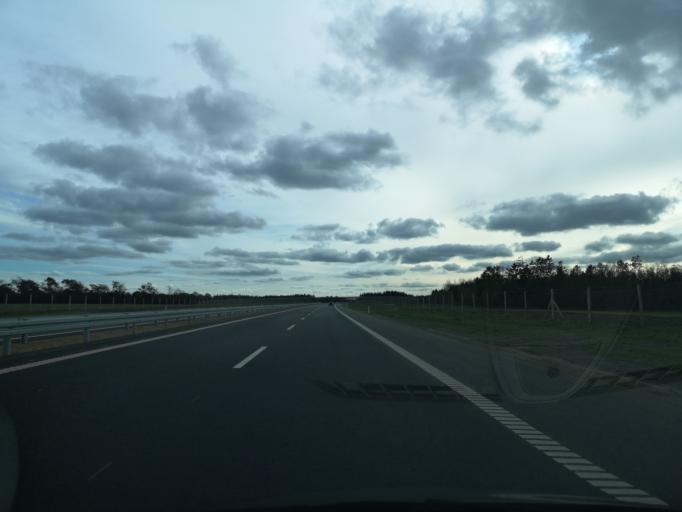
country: DK
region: Central Jutland
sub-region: Herning Kommune
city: Avlum
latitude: 56.3425
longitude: 8.7379
